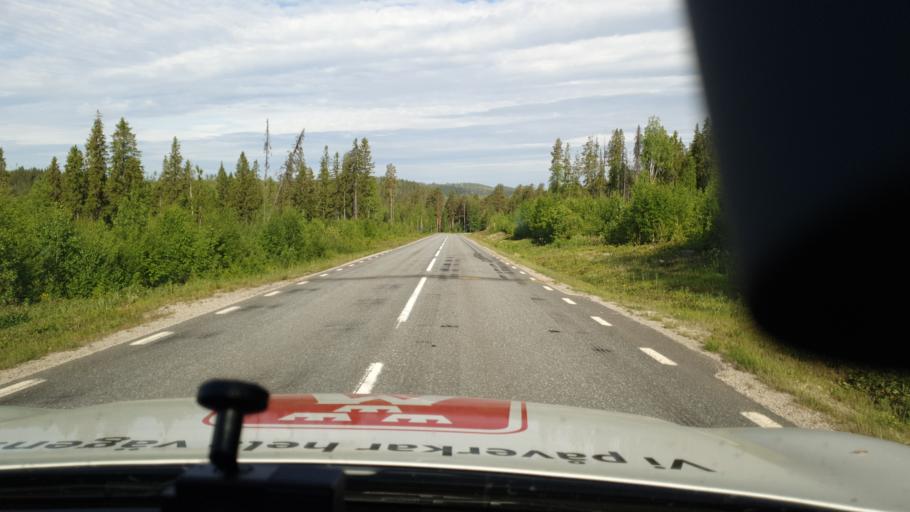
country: SE
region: Vaesterbotten
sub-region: Lycksele Kommun
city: Lycksele
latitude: 64.4279
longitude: 18.9885
